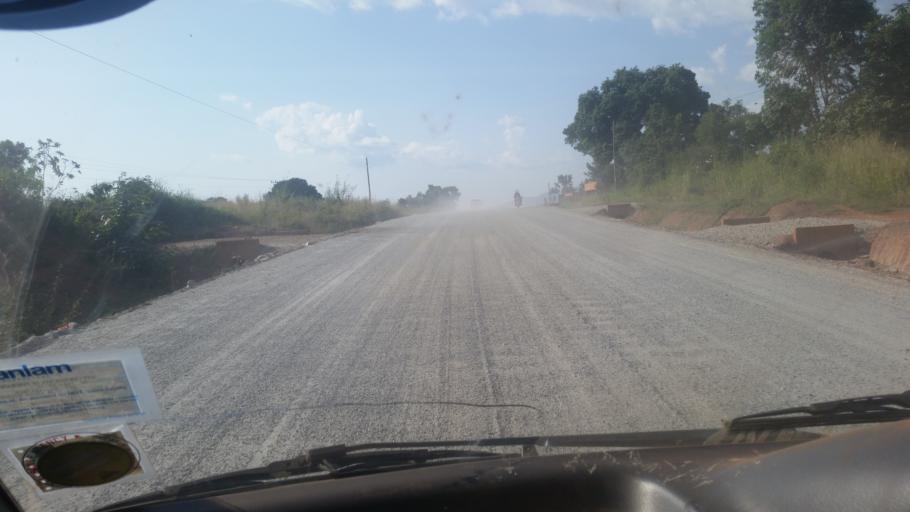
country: UG
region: Western Region
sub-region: Hoima District
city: Hoima
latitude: 1.3950
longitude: 31.3321
